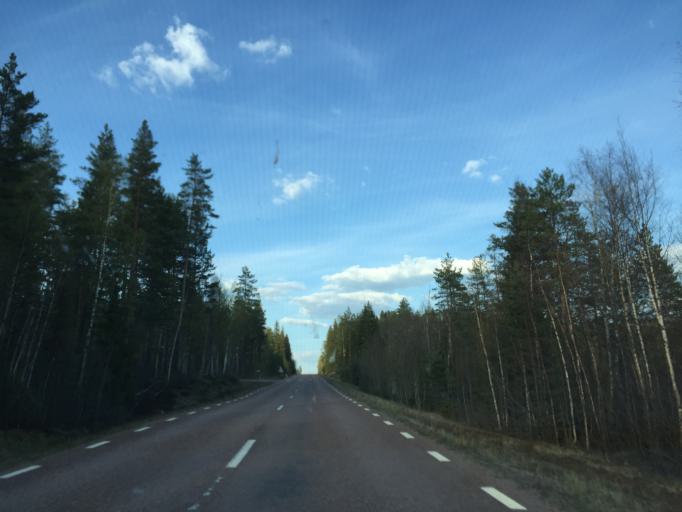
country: SE
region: Dalarna
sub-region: Leksand Municipality
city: Siljansnas
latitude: 60.6709
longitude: 14.6566
